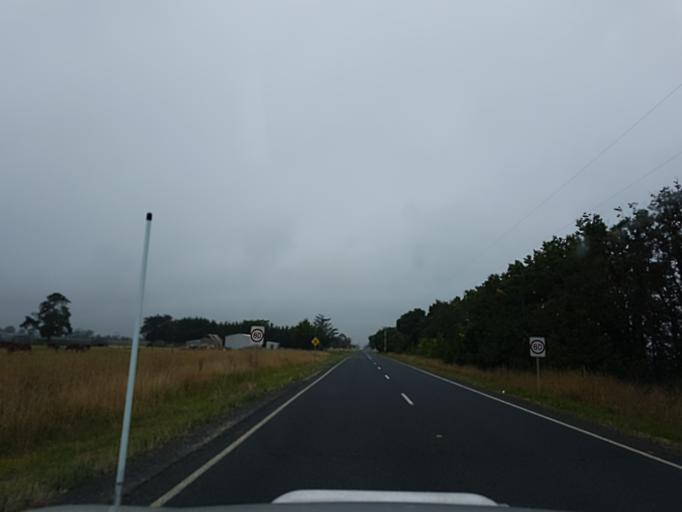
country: AU
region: Victoria
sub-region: Wellington
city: Sale
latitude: -38.0663
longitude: 147.0606
